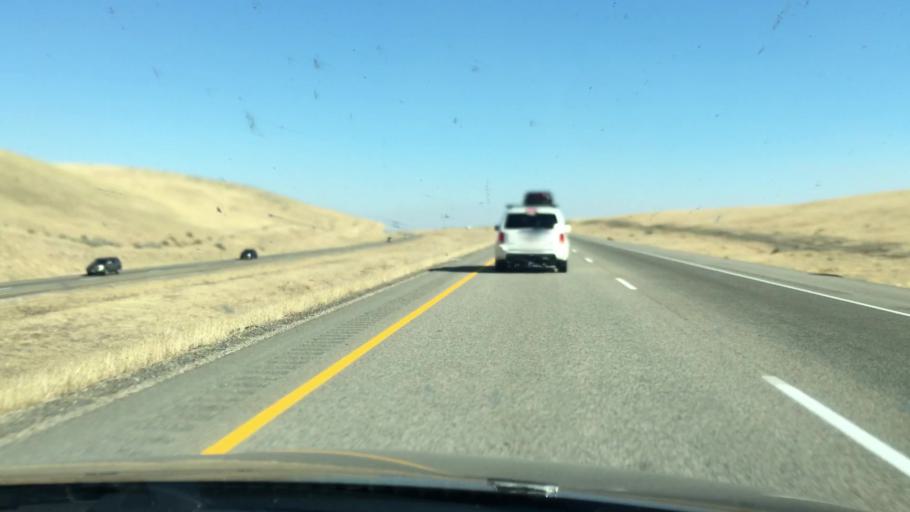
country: US
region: Idaho
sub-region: Ada County
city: Boise
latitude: 43.4932
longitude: -116.1284
